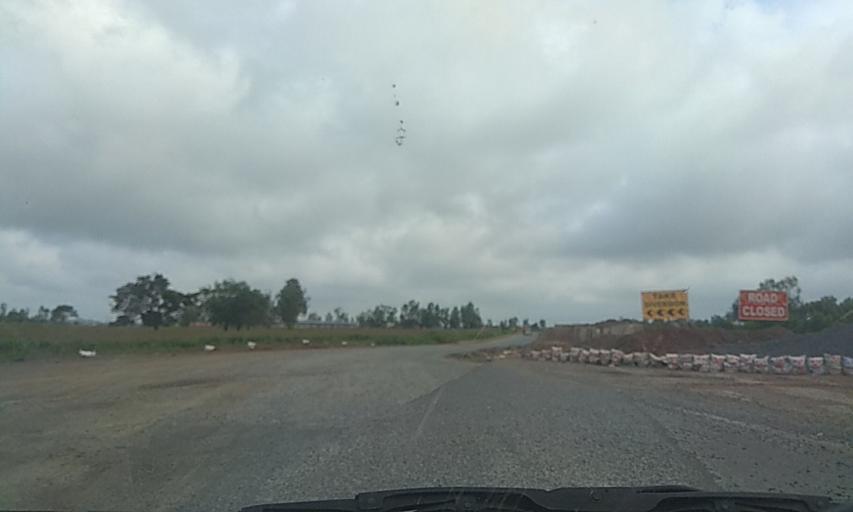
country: IN
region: Karnataka
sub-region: Haveri
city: Shiggaon
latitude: 15.0972
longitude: 75.1524
